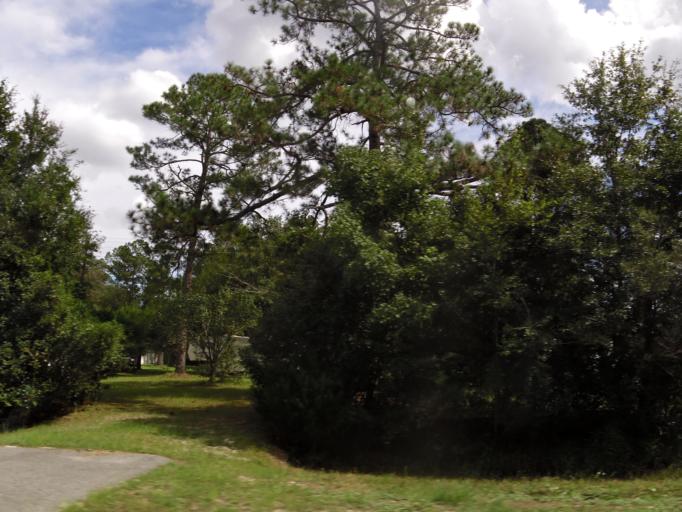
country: US
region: Georgia
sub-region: Brantley County
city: Nahunta
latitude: 31.1641
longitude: -81.9909
